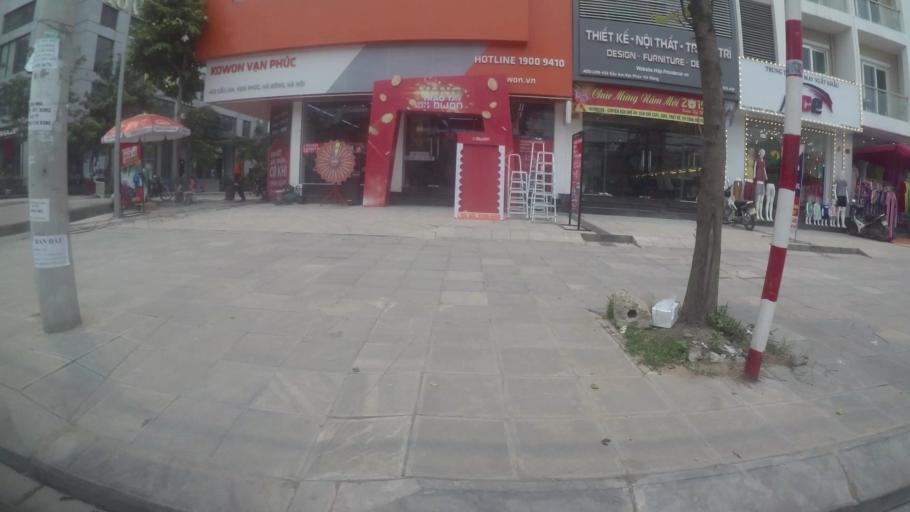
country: VN
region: Ha Noi
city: Ha Dong
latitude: 20.9773
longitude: 105.7754
